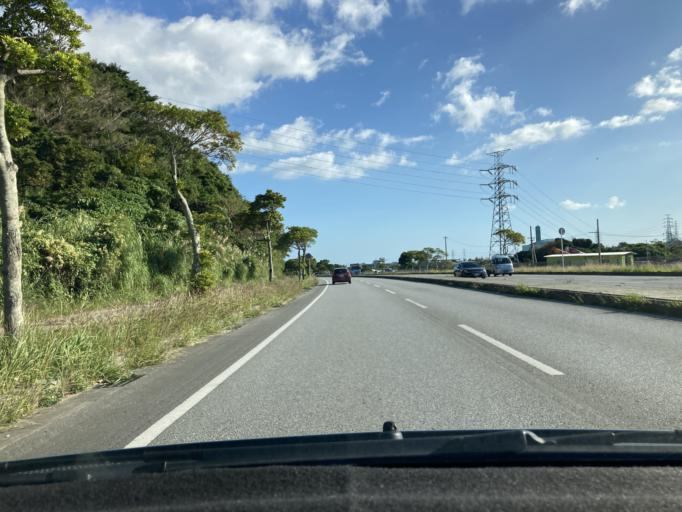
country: JP
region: Okinawa
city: Ishikawa
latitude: 26.4060
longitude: 127.8218
